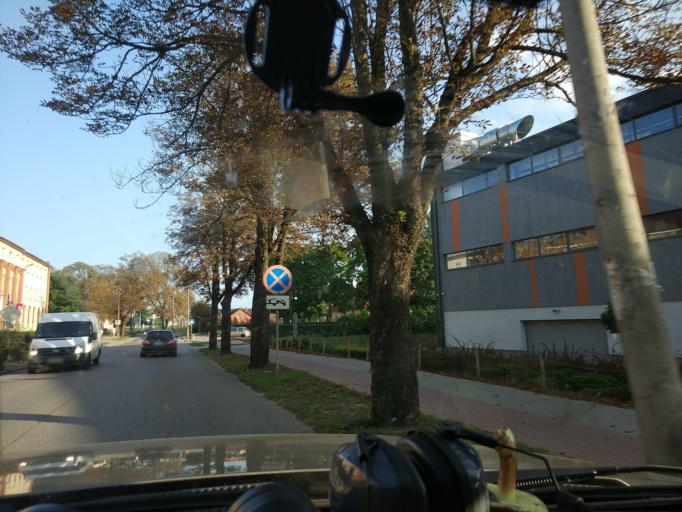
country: PL
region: Warmian-Masurian Voivodeship
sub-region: Powiat szczycienski
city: Szczytno
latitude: 53.5624
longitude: 20.9896
